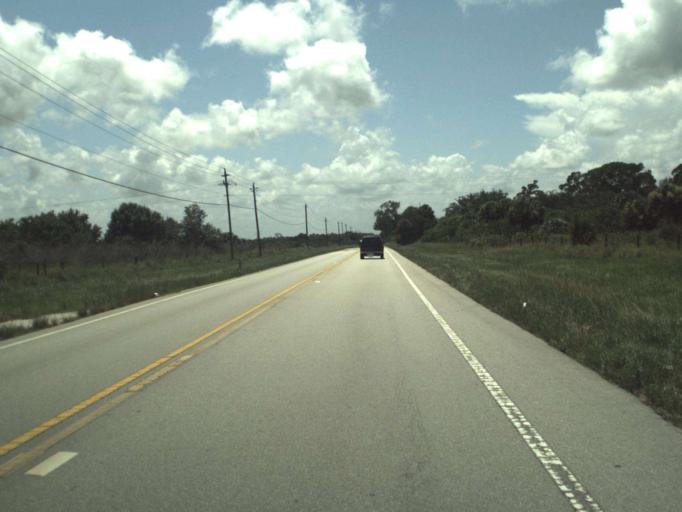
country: US
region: Florida
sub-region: Indian River County
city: Sebastian
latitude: 27.7488
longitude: -80.4897
